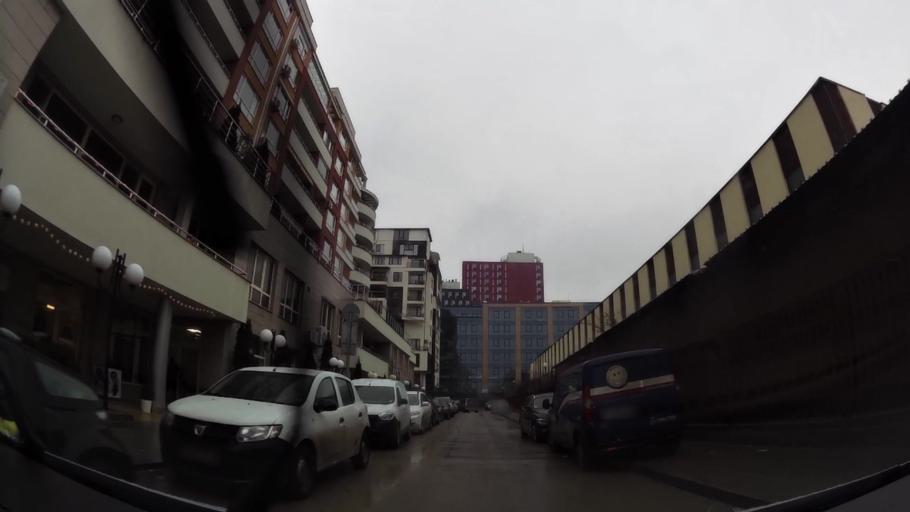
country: BG
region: Sofia-Capital
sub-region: Stolichna Obshtina
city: Sofia
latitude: 42.6630
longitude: 23.3820
